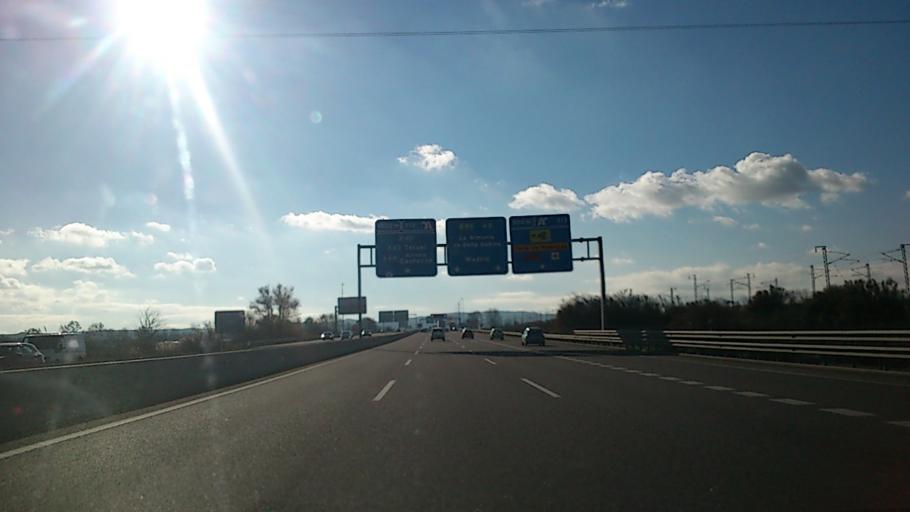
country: ES
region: Aragon
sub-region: Provincia de Zaragoza
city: Oliver-Valdefierro, Oliver, Valdefierro
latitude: 41.6508
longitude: -0.9614
